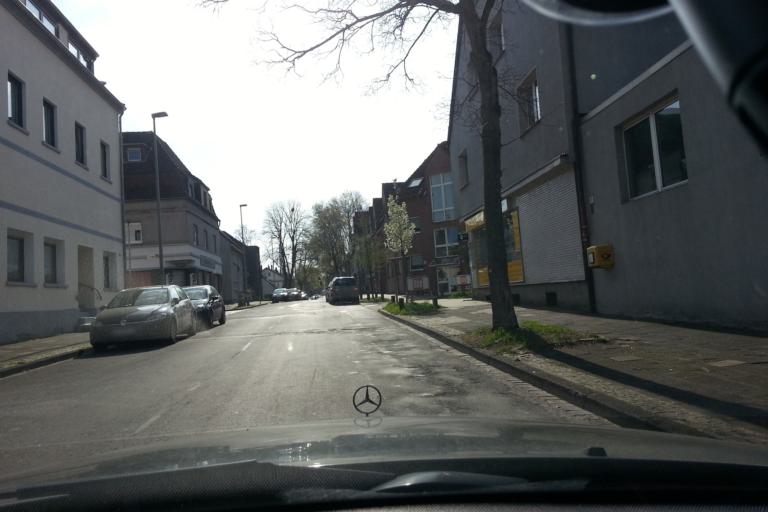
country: DE
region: North Rhine-Westphalia
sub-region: Regierungsbezirk Arnsberg
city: Herne
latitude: 51.5386
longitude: 7.1931
